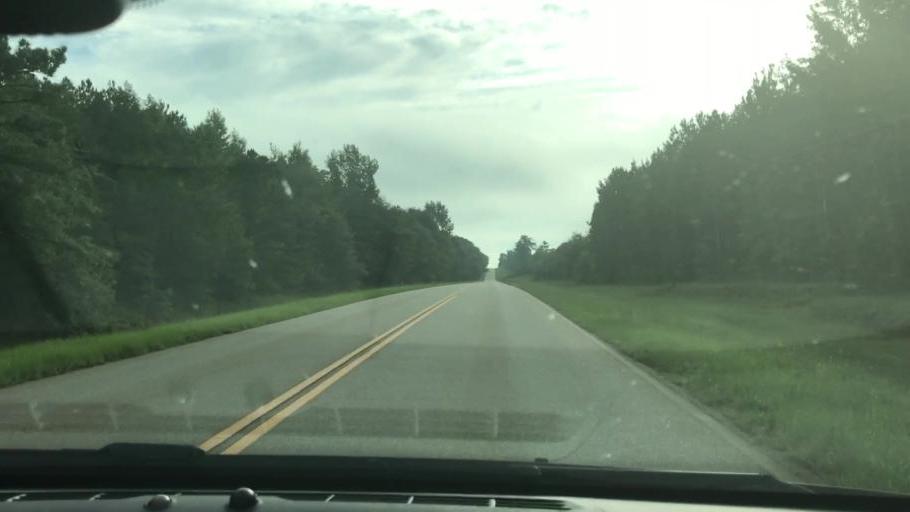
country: US
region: Georgia
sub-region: Stewart County
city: Lumpkin
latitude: 31.9779
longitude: -84.9555
